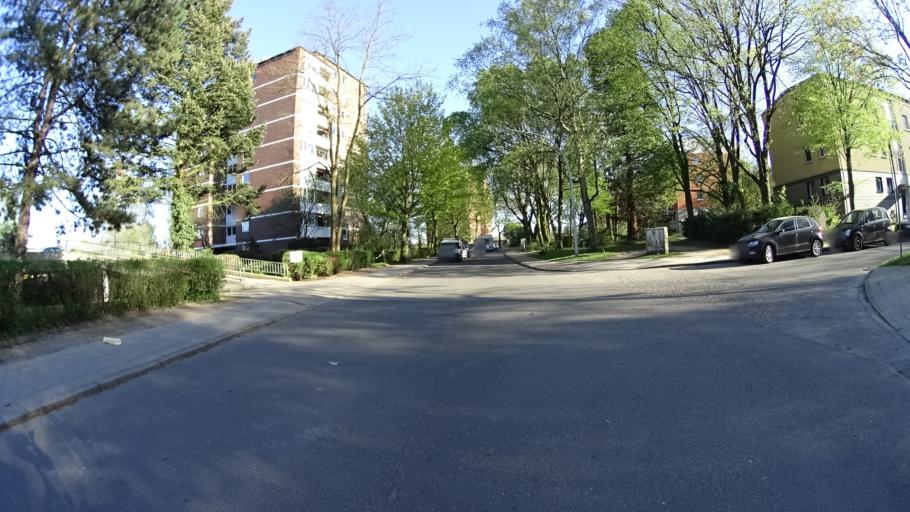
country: DE
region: Hamburg
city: Stellingen
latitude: 53.5902
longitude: 9.9377
